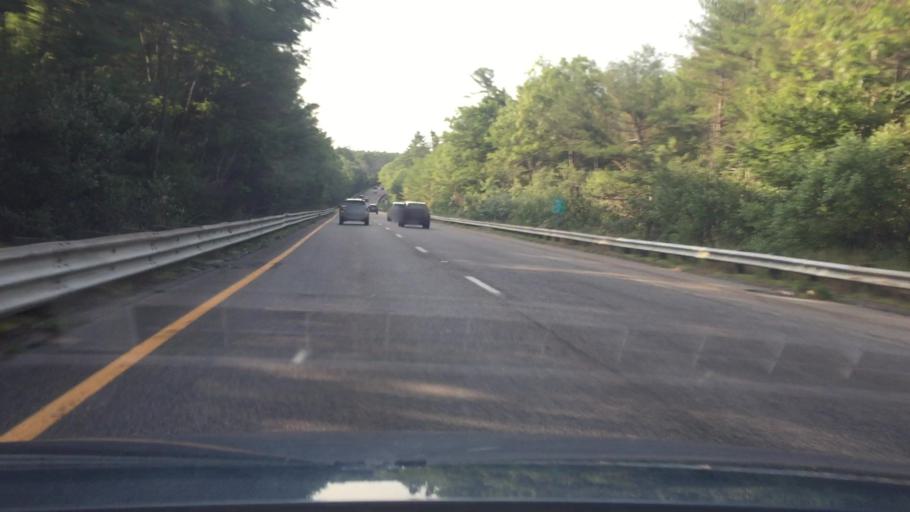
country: US
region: Massachusetts
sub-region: Plymouth County
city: North Pembroke
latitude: 42.1022
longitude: -70.7584
